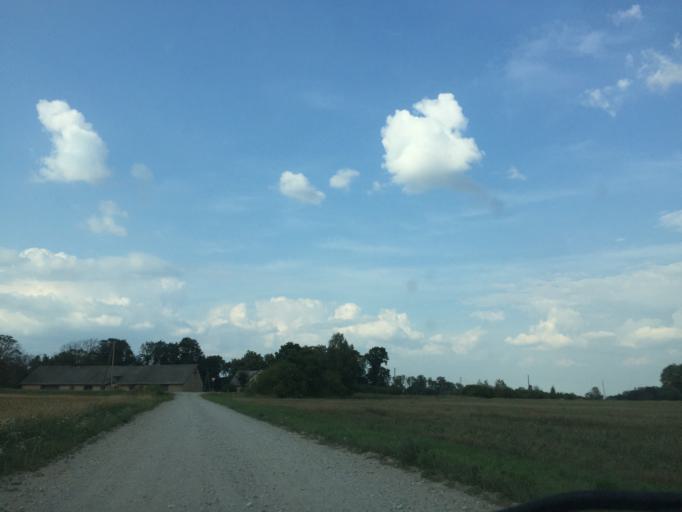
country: LT
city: Zagare
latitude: 56.4815
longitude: 23.1510
